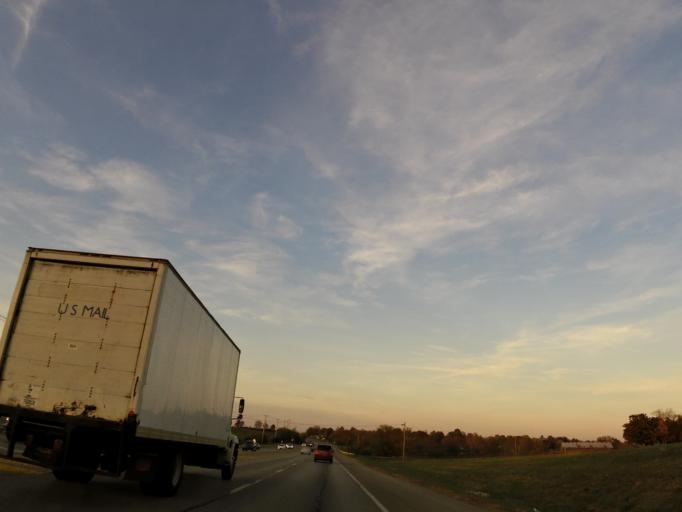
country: US
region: Kentucky
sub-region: Fayette County
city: Monticello
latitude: 37.9583
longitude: -84.5379
